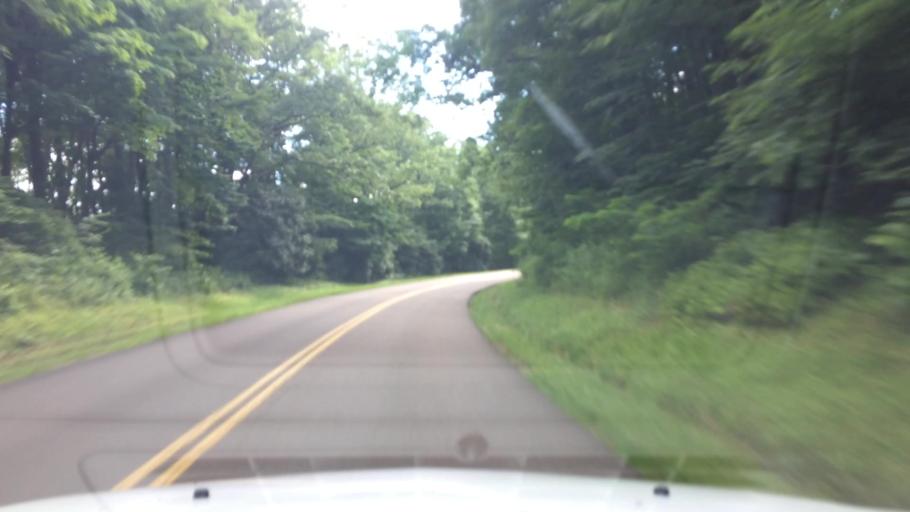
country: US
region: North Carolina
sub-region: Watauga County
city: Blowing Rock
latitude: 36.1563
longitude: -81.6742
